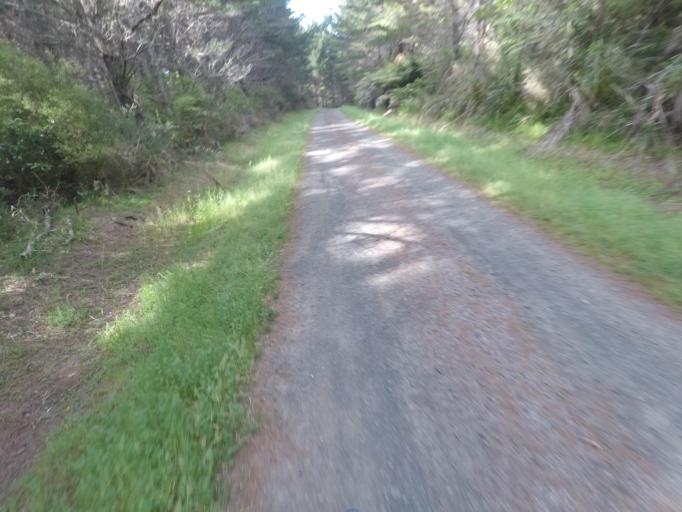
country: NZ
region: Auckland
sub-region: Auckland
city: Muriwai Beach
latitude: -36.7451
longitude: 174.5653
